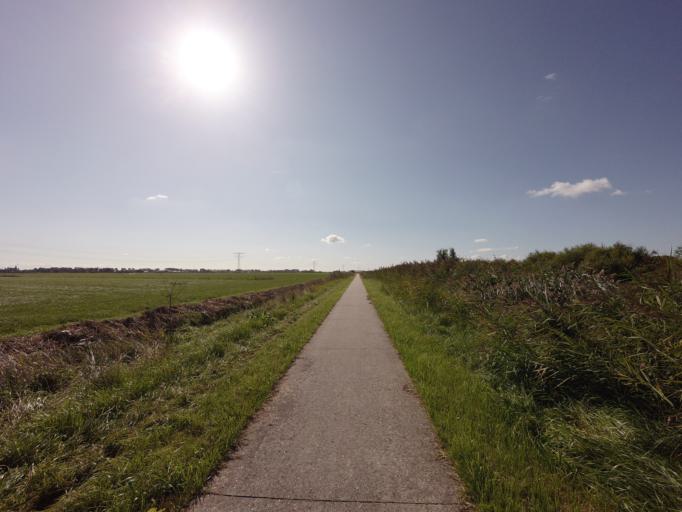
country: NL
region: Friesland
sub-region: Gemeente Boarnsterhim
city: Reduzum
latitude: 53.1474
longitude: 5.7637
